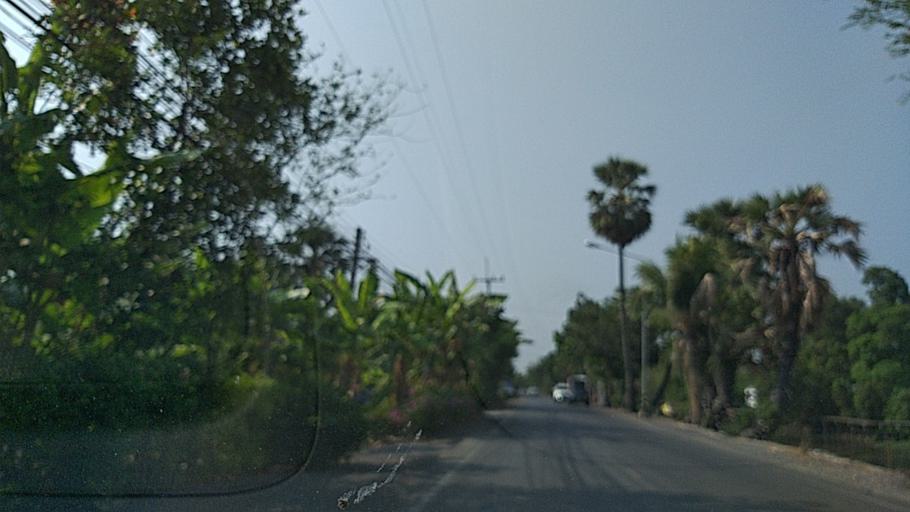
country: TH
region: Pathum Thani
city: Lam Luk Ka
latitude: 13.9490
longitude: 100.7059
